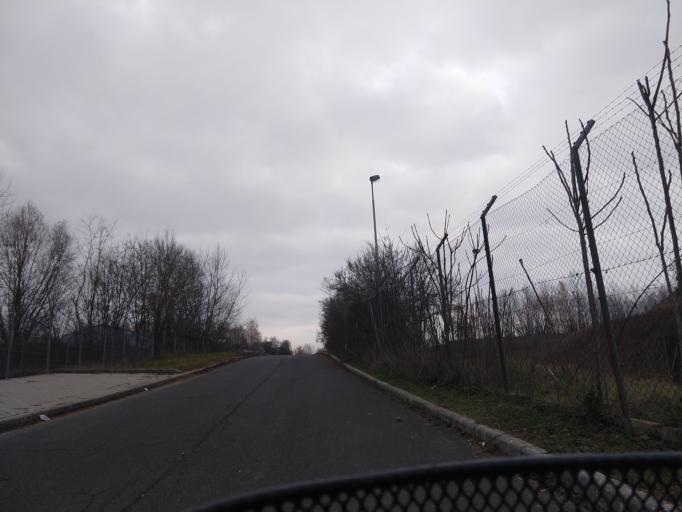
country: HU
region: Pest
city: Orbottyan
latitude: 47.6658
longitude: 19.2841
